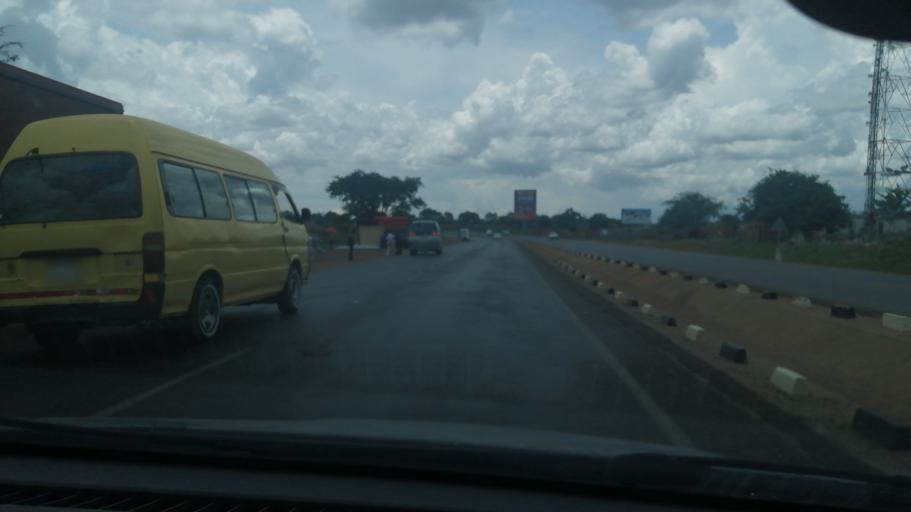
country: ZW
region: Harare
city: Harare
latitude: -17.8185
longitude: 30.9382
